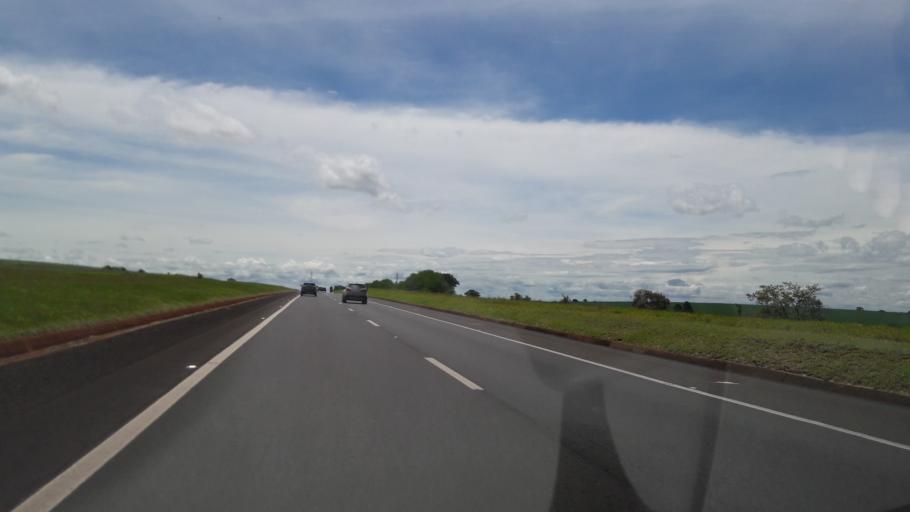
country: BR
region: Sao Paulo
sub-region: Avare
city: Avare
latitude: -22.9561
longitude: -48.8431
